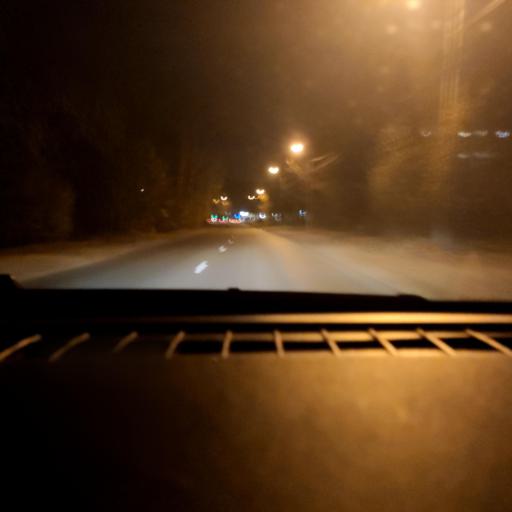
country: RU
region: Voronezj
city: Voronezh
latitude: 51.7235
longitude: 39.2167
